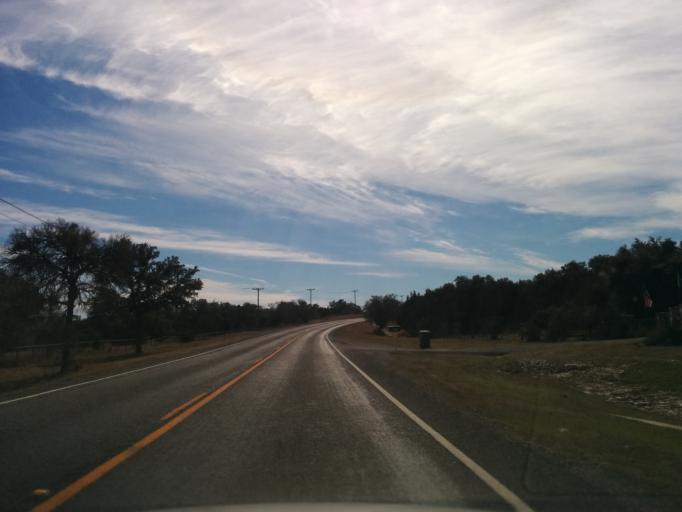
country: US
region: Texas
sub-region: Bexar County
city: Fair Oaks Ranch
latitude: 29.8878
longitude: -98.5570
